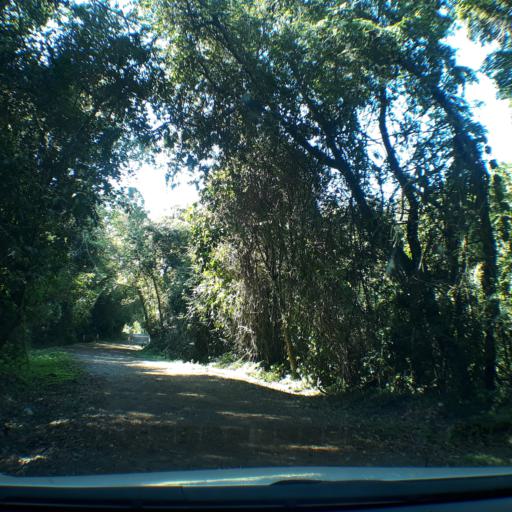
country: AR
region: Misiones
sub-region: Departamento de San Ignacio
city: San Ignacio
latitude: -27.2825
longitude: -55.5640
